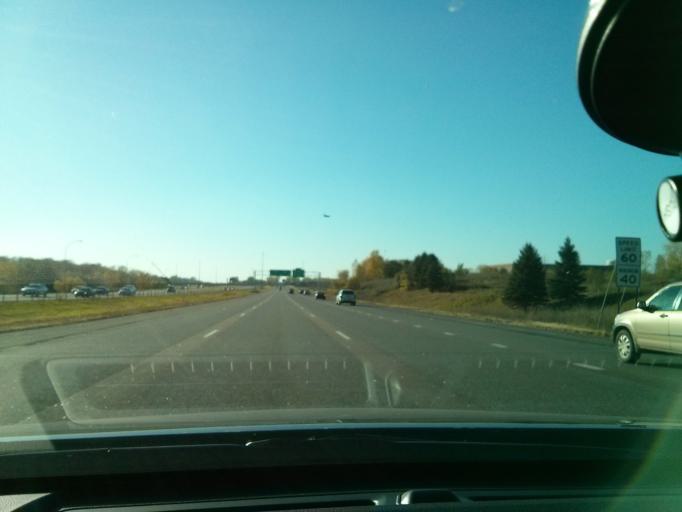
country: US
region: Minnesota
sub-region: Dakota County
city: Mendota Heights
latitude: 44.8629
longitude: -93.1325
